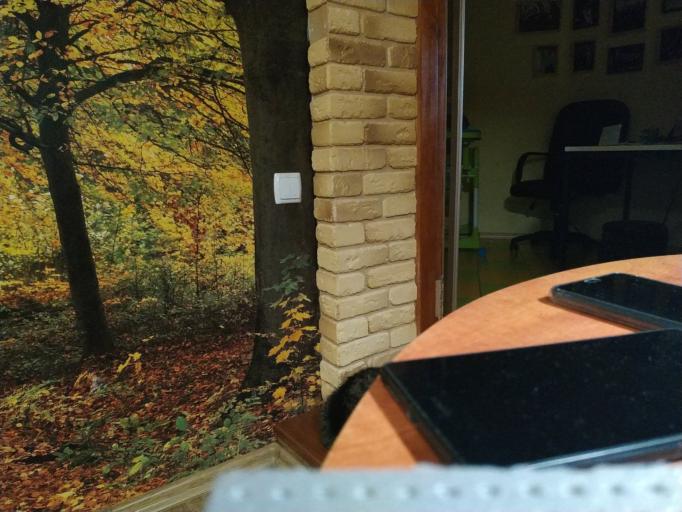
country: RU
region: Tverskaya
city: Zubtsov
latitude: 56.3608
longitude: 34.6641
